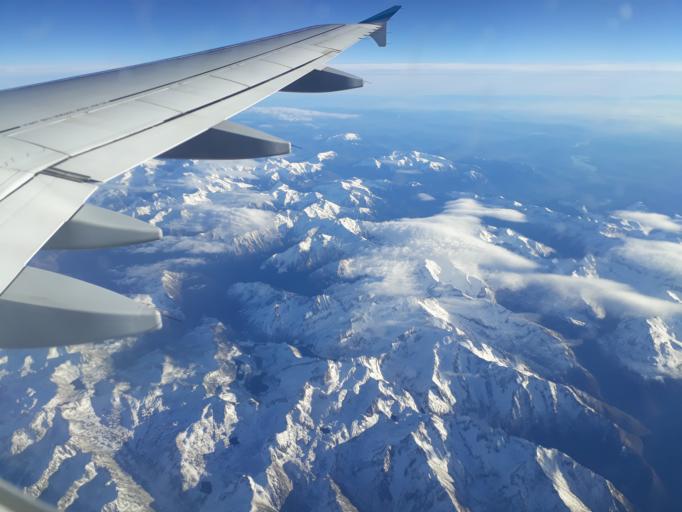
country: FR
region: Midi-Pyrenees
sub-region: Departement des Hautes-Pyrenees
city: Luz-Saint-Sauveur
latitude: 42.9312
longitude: 0.0147
